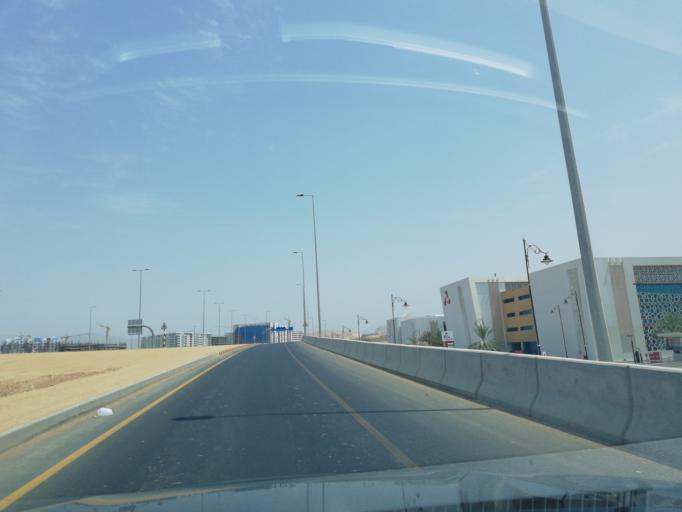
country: OM
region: Muhafazat Masqat
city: Bawshar
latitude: 23.5811
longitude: 58.2933
